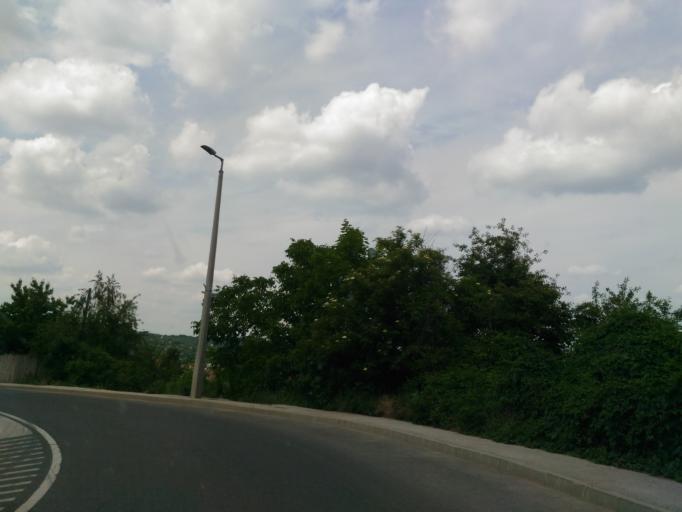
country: HU
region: Baranya
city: Komlo
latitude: 46.1875
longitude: 18.2616
